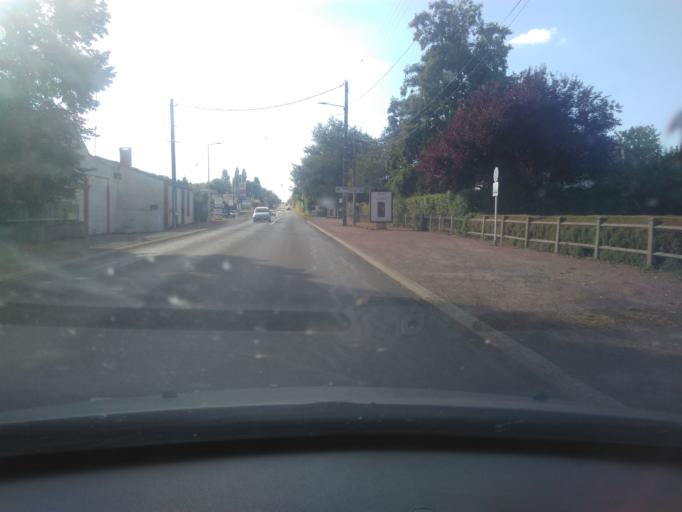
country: FR
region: Pays de la Loire
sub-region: Departement de la Vendee
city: Saint-Florent-des-Bois
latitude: 46.5953
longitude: -1.3186
